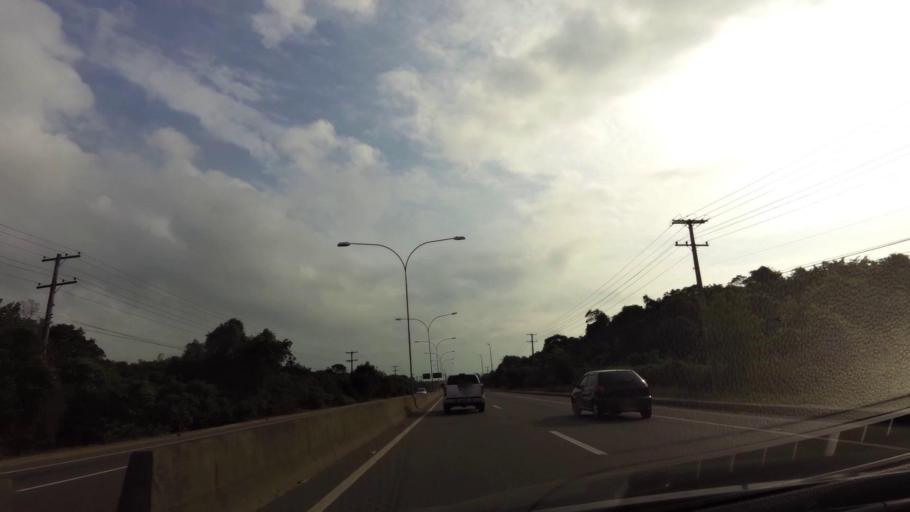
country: BR
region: Espirito Santo
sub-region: Vila Velha
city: Vila Velha
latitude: -20.4147
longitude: -40.3279
